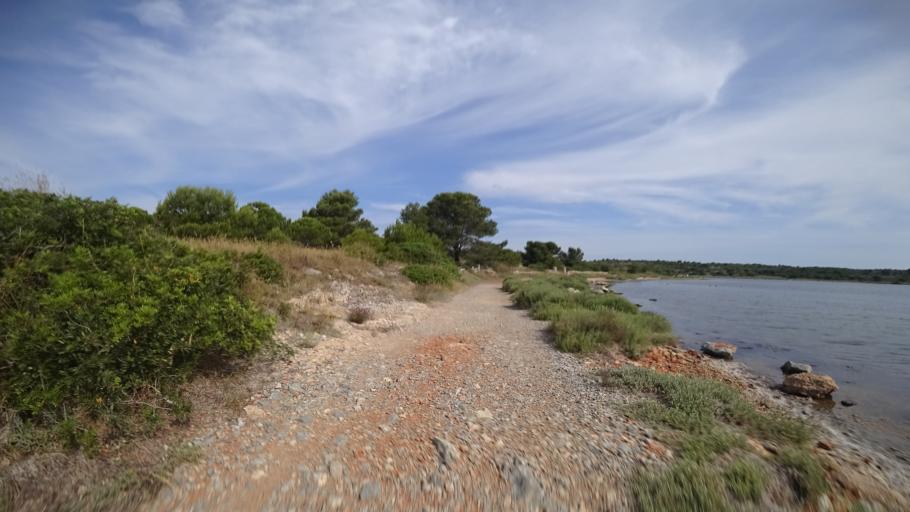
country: FR
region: Languedoc-Roussillon
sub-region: Departement de l'Aude
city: Leucate
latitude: 42.9015
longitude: 3.0391
